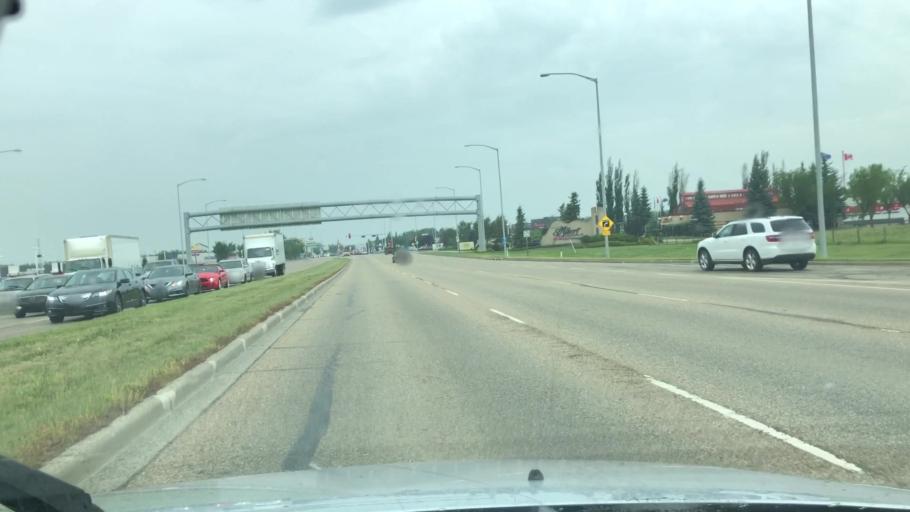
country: CA
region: Alberta
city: St. Albert
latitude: 53.6184
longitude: -113.6032
